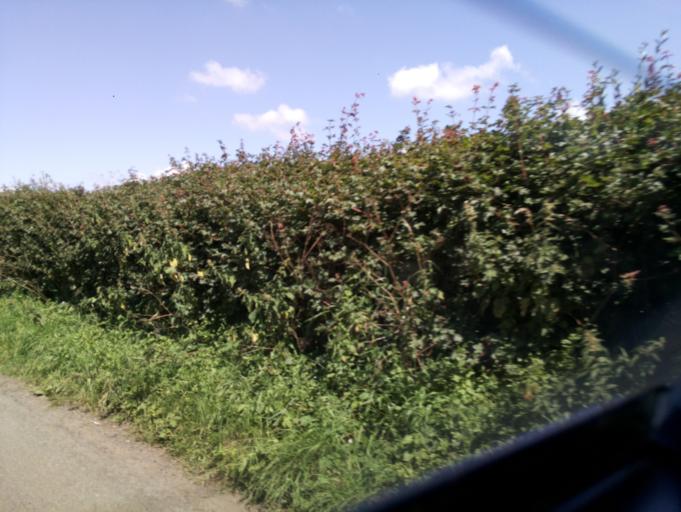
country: GB
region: England
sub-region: Wiltshire
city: Norton
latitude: 51.5196
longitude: -2.1328
